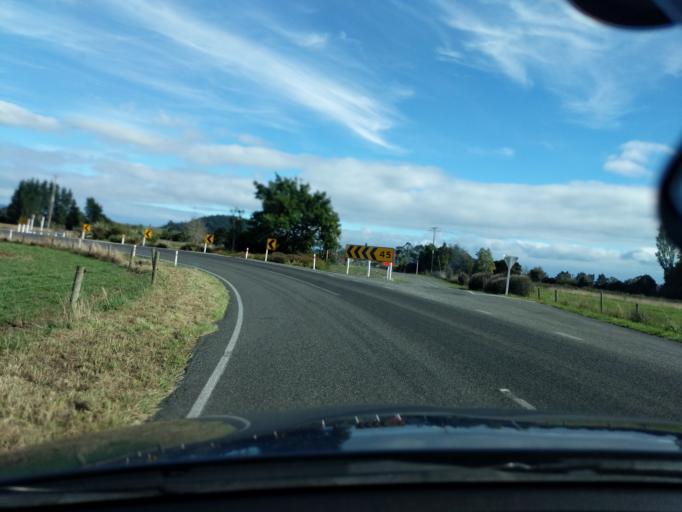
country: NZ
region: Tasman
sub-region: Tasman District
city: Takaka
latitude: -40.8466
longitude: 172.8387
